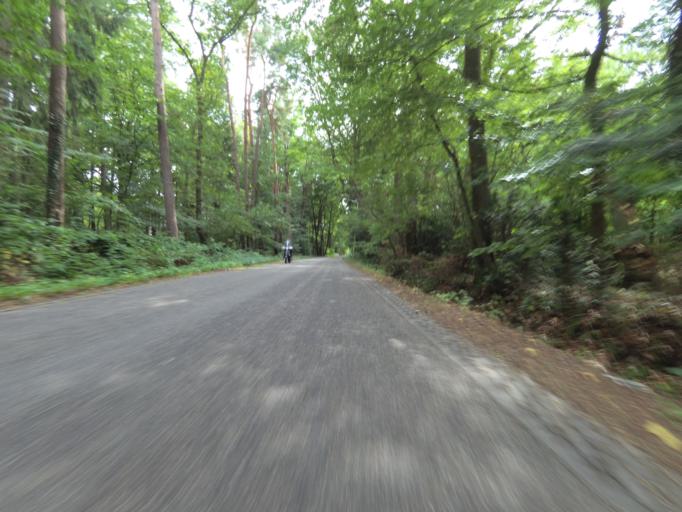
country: NL
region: Overijssel
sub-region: Gemeente Hengelo
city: Hengelo
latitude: 52.2485
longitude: 6.8458
